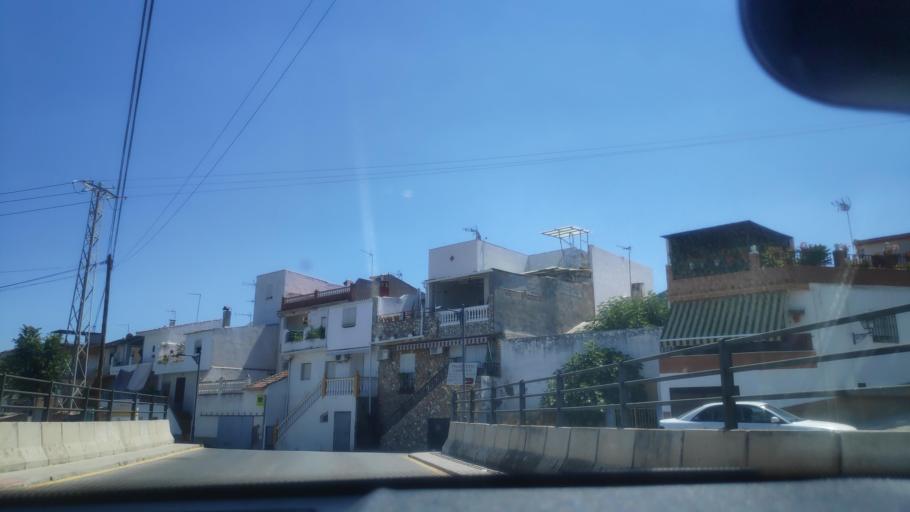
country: ES
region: Andalusia
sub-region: Provincia de Granada
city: Alhendin
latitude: 37.1044
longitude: -3.6467
